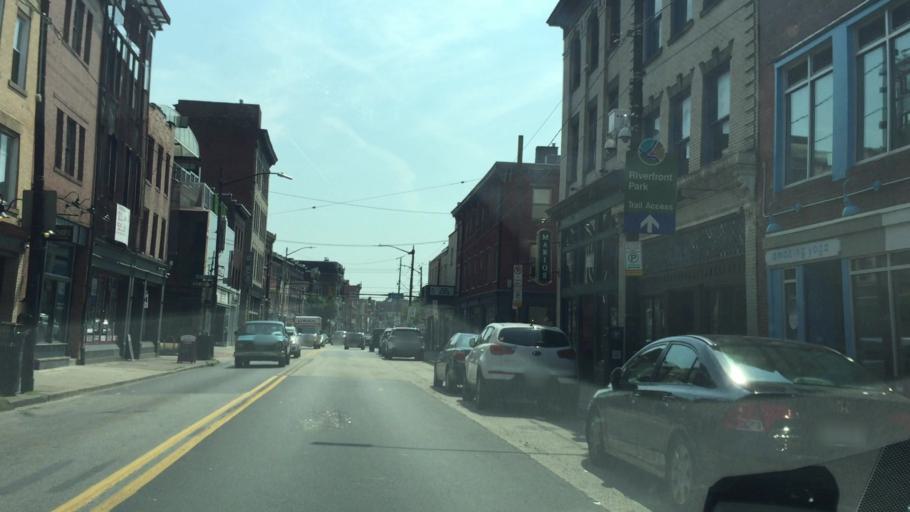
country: US
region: Pennsylvania
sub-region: Allegheny County
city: Mount Oliver
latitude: 40.4288
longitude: -79.9832
